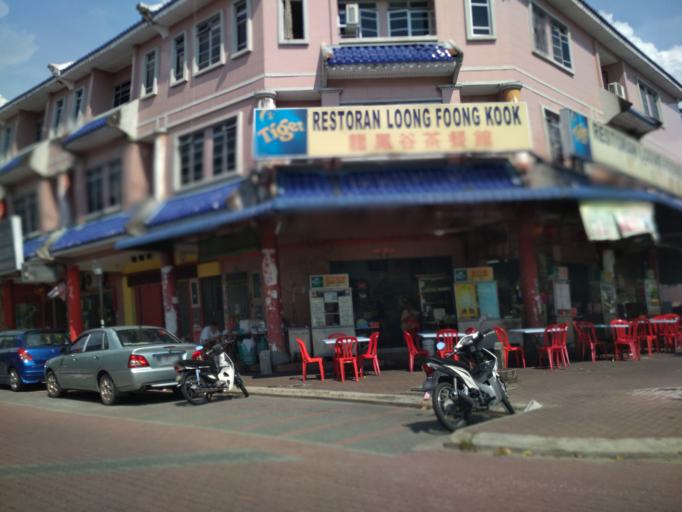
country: MY
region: Perak
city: Kampar
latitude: 4.3270
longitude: 101.1431
